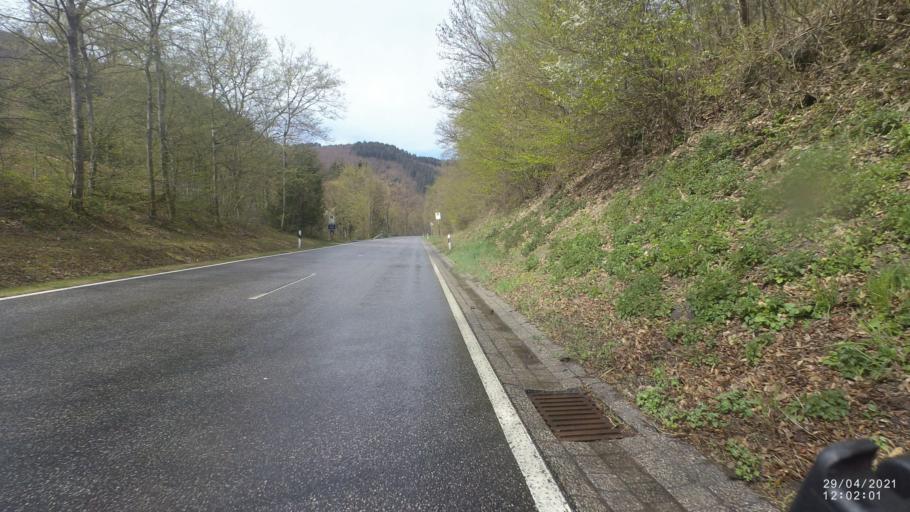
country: DE
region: Rheinland-Pfalz
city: Sankt Johann
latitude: 50.3438
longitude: 7.1941
